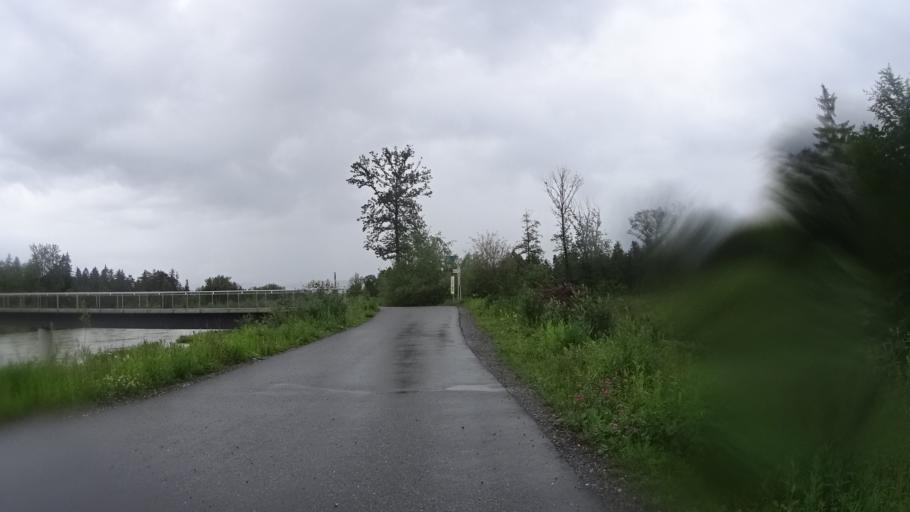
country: CH
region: Saint Gallen
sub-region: Wahlkreis Rheintal
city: Ruthi
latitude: 47.2938
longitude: 9.5568
